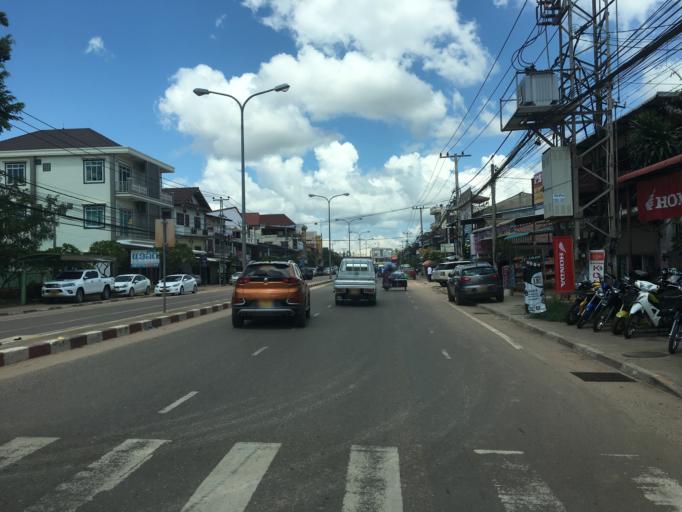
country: TH
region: Nong Khai
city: Si Chiang Mai
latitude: 17.9740
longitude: 102.5605
